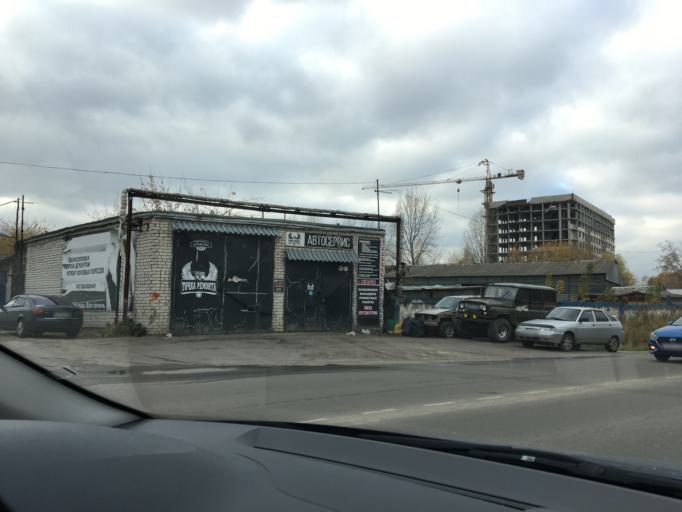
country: RU
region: Nizjnij Novgorod
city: Kstovo
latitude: 56.1598
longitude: 44.2067
